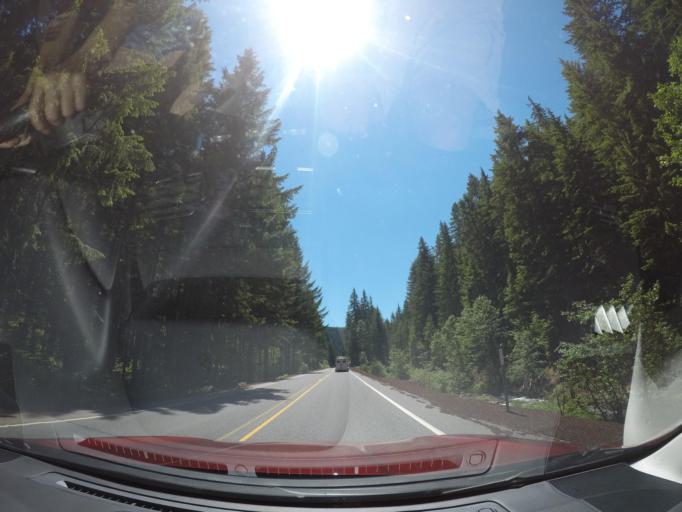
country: US
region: Oregon
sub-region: Linn County
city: Mill City
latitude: 44.5600
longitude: -121.9986
